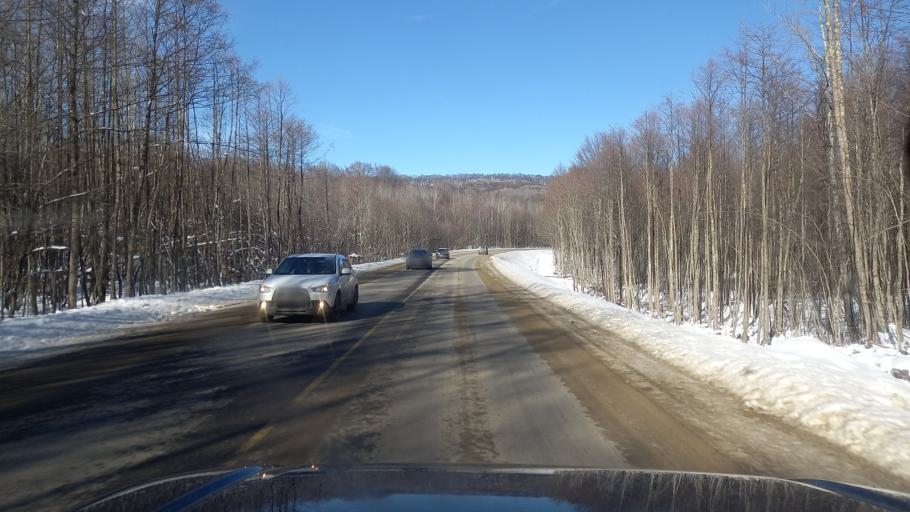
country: RU
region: Adygeya
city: Kamennomostskiy
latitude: 44.2113
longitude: 40.0774
